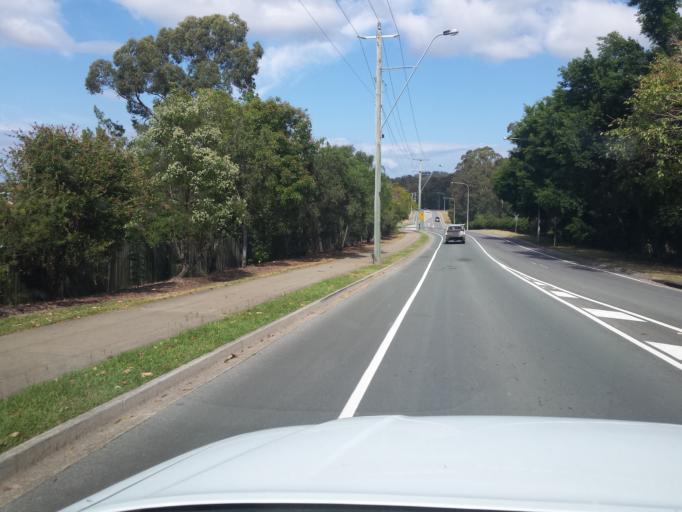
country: AU
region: Queensland
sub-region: Moreton Bay
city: Ferny Hills
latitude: -27.3816
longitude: 152.9476
